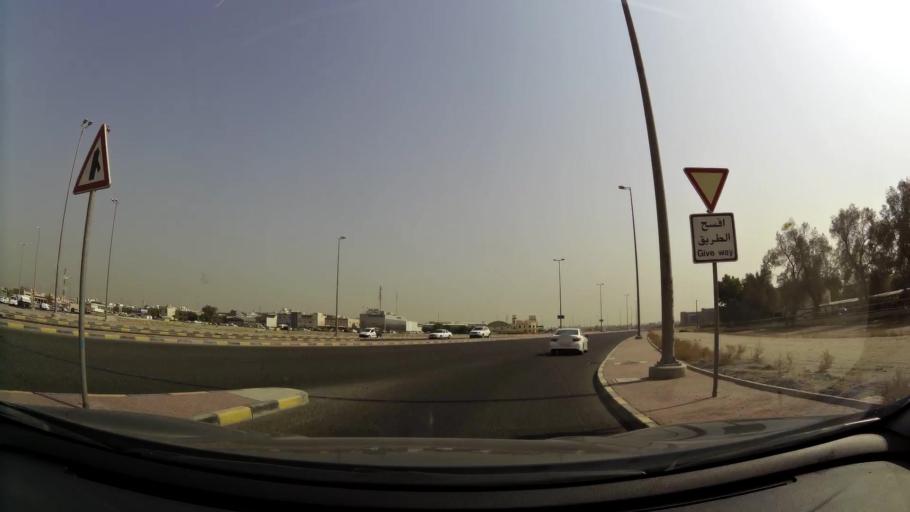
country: KW
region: Al Asimah
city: Ar Rabiyah
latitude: 29.2889
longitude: 47.9149
